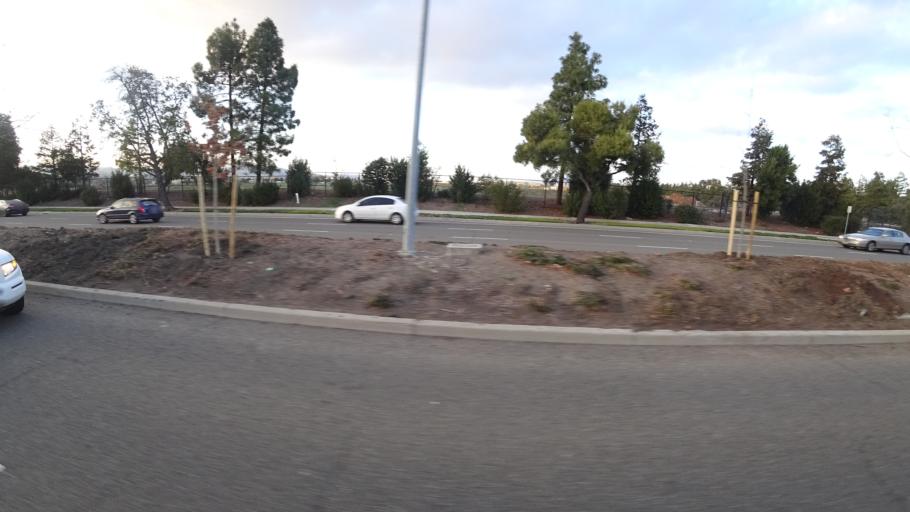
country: US
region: California
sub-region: Alameda County
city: Dublin
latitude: 37.6904
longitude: -121.9108
